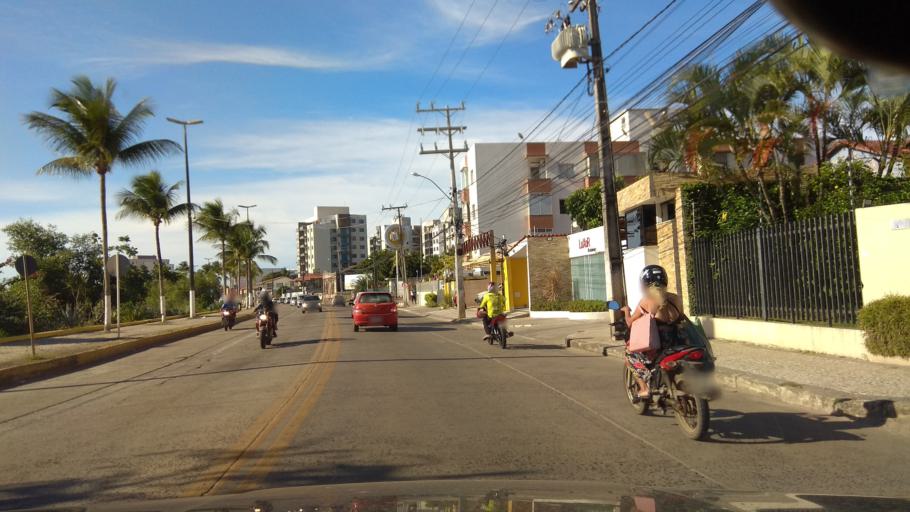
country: BR
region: Bahia
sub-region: Ilheus
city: Ilheus
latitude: -14.8090
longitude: -39.0355
